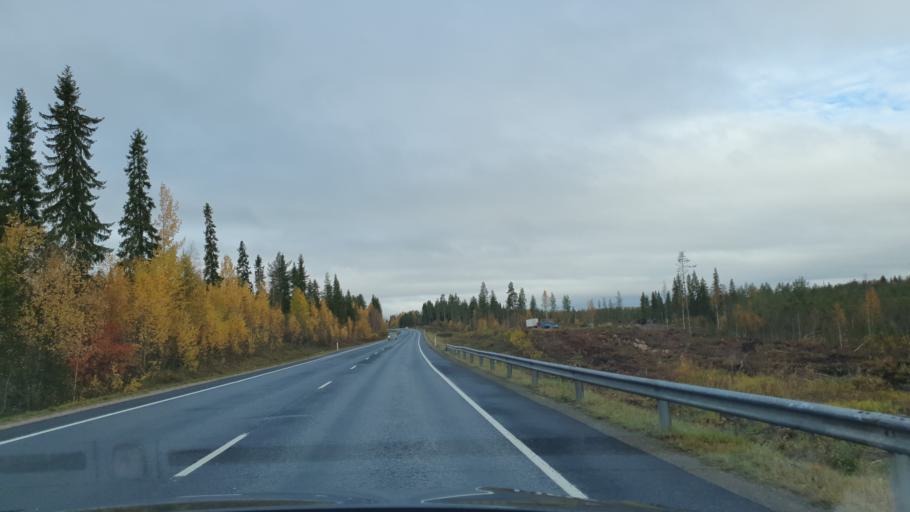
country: FI
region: Lapland
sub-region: Rovaniemi
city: Rovaniemi
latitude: 66.6172
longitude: 25.5461
